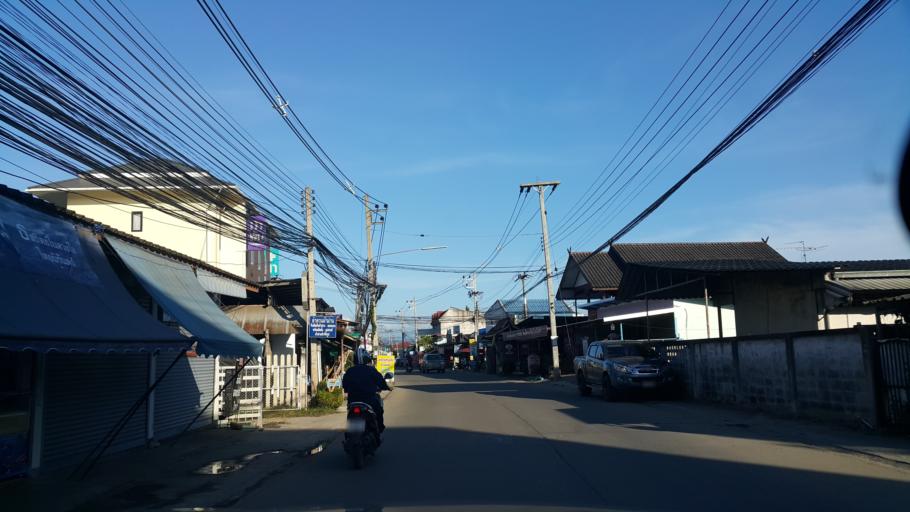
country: TH
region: Lamphun
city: Lamphun
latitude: 18.5999
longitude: 99.0247
